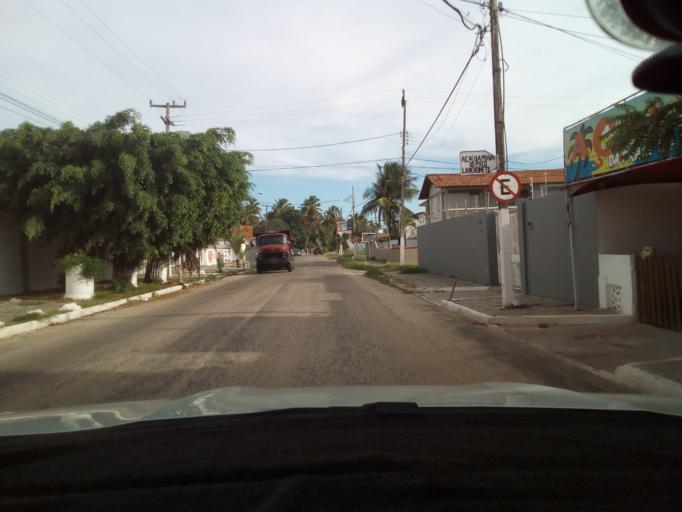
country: BR
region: Paraiba
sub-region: Cabedelo
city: Cabedelo
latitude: -7.0249
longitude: -34.8306
